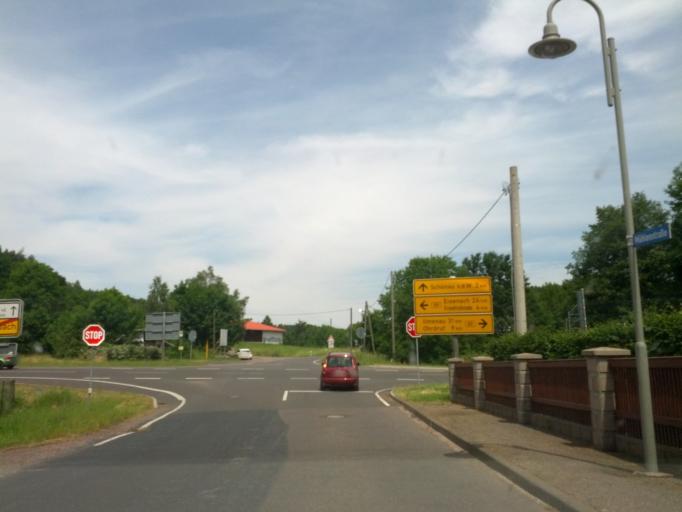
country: DE
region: Thuringia
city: Ernstroda
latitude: 50.8489
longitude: 10.6149
